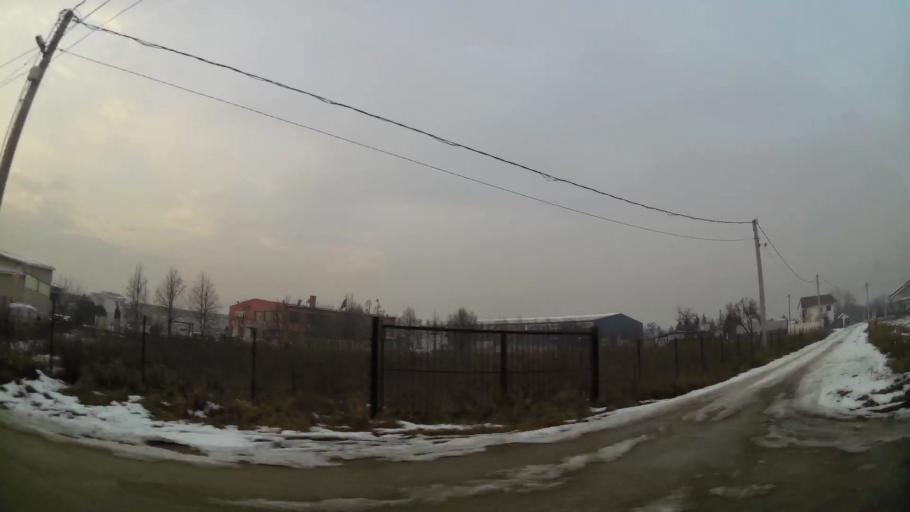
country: MK
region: Suto Orizari
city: Suto Orizare
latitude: 42.0337
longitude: 21.4057
